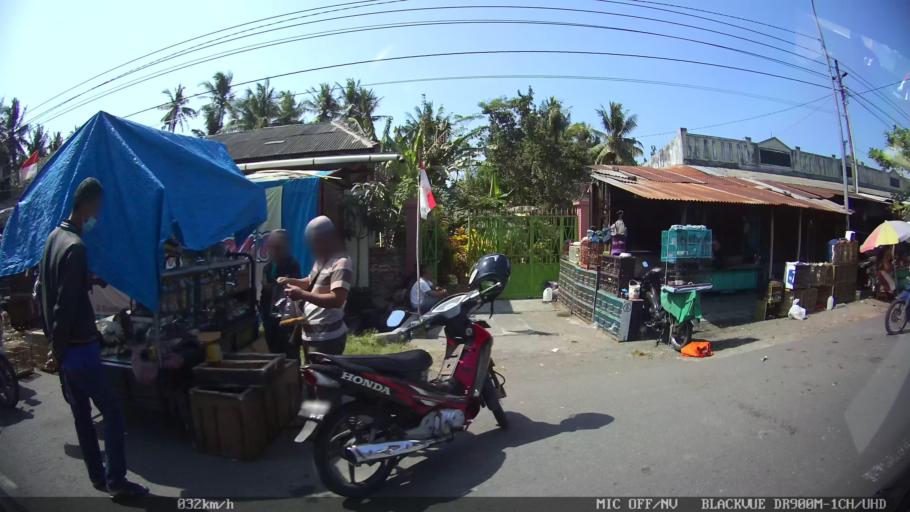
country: ID
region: Daerah Istimewa Yogyakarta
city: Srandakan
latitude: -7.9488
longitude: 110.2217
